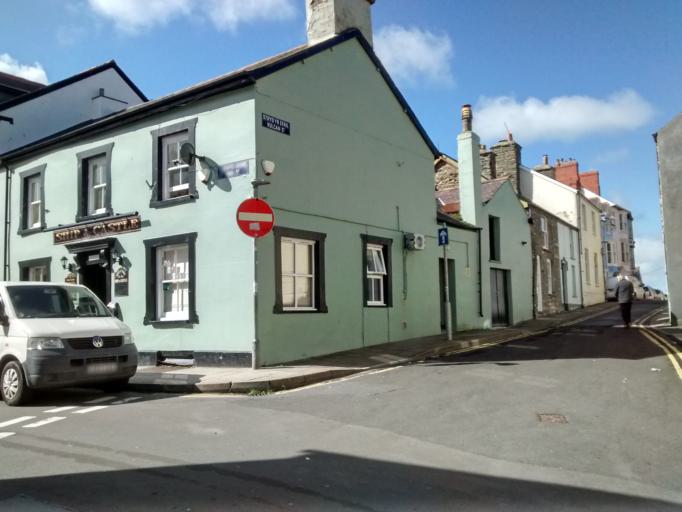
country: GB
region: Wales
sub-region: County of Ceredigion
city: Aberystwyth
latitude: 52.4134
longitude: -4.0867
